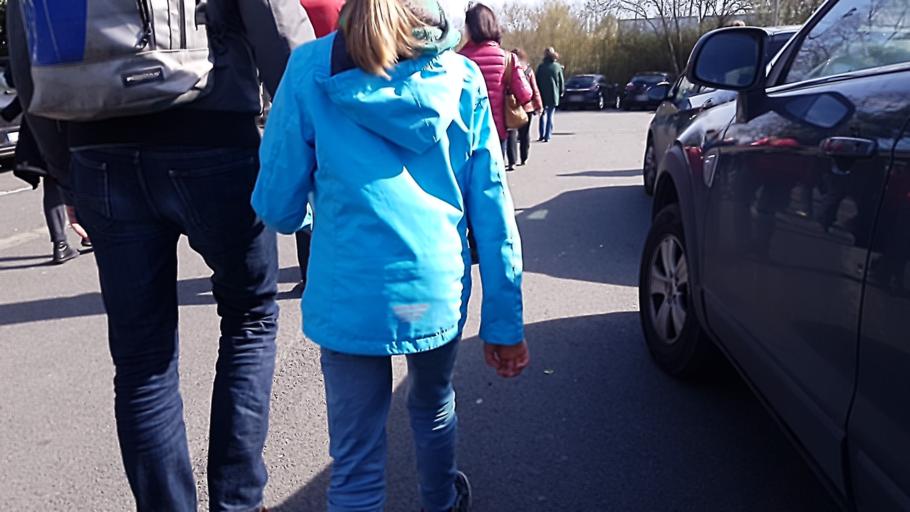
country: BE
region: Flanders
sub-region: Provincie West-Vlaanderen
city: Kortrijk
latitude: 50.8167
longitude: 3.2851
